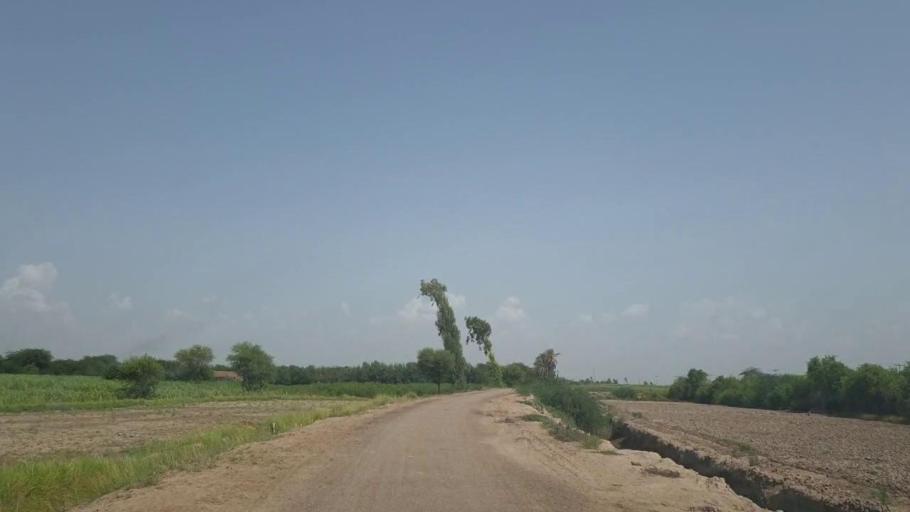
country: PK
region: Sindh
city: Tando Bago
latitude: 24.7572
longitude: 69.1768
